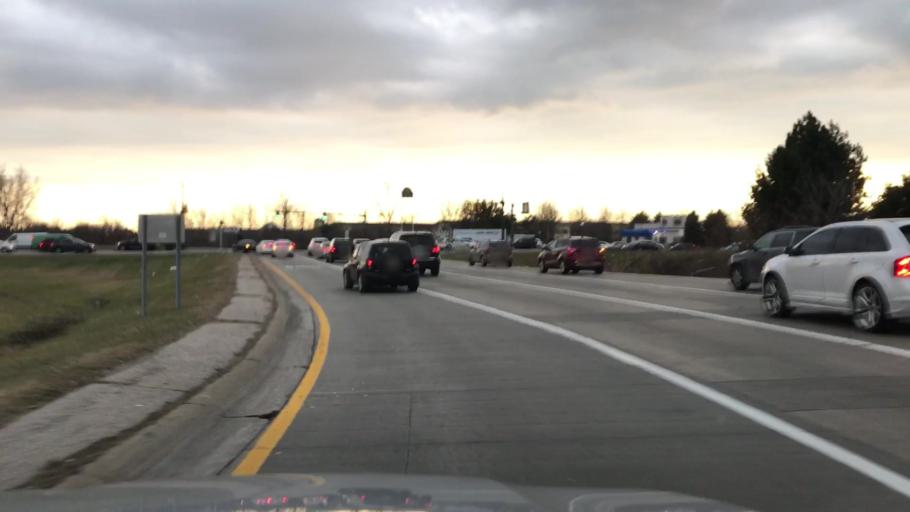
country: US
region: Michigan
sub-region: Wayne County
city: Canton
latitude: 42.3240
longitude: -83.4459
